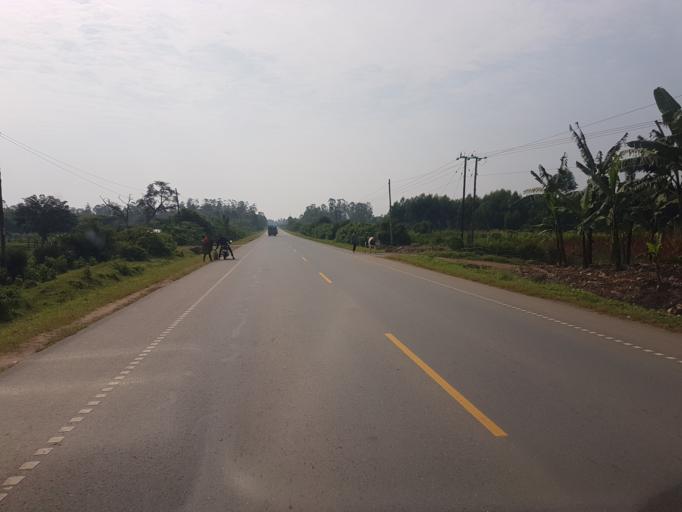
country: UG
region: Western Region
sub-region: Sheema District
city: Kibingo
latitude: -0.6351
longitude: 30.5229
